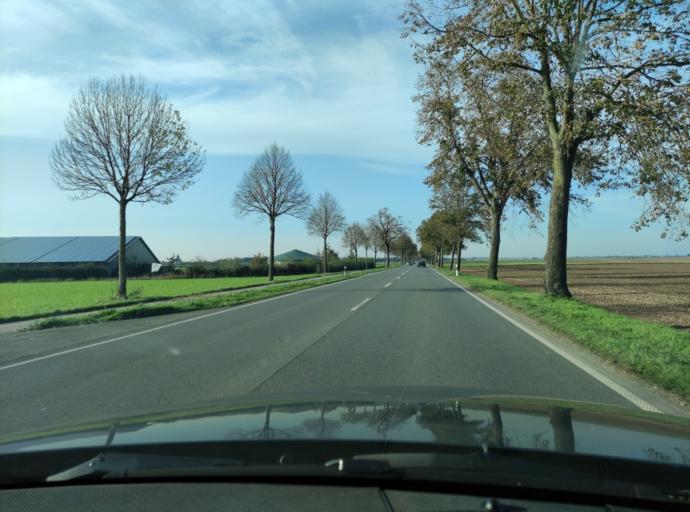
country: DE
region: North Rhine-Westphalia
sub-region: Regierungsbezirk Dusseldorf
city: Rheurdt
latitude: 51.4189
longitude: 6.4664
